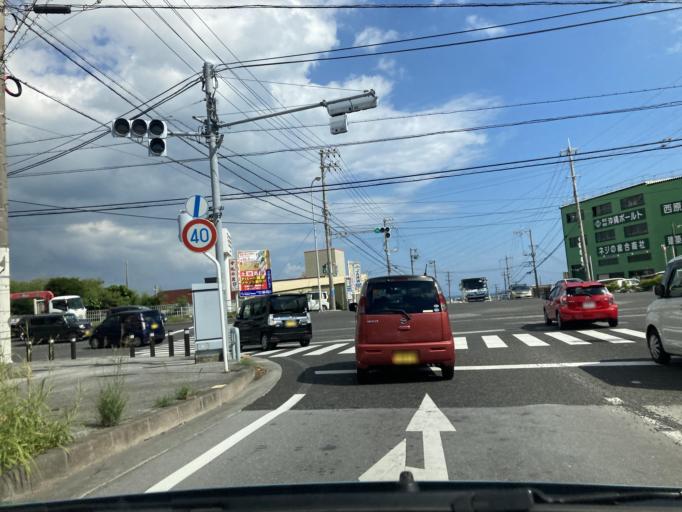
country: JP
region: Okinawa
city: Ginowan
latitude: 26.2329
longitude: 127.7693
